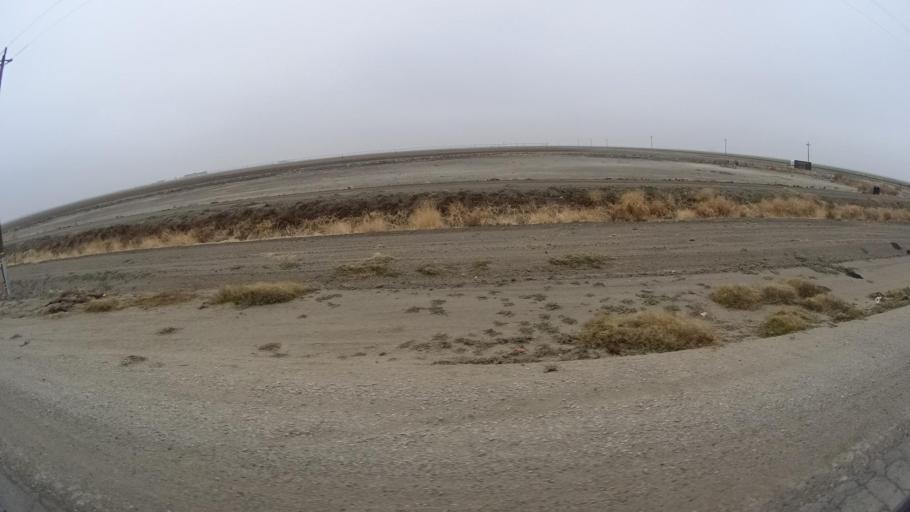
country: US
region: California
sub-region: Kern County
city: Rosedale
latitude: 35.1790
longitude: -119.1991
